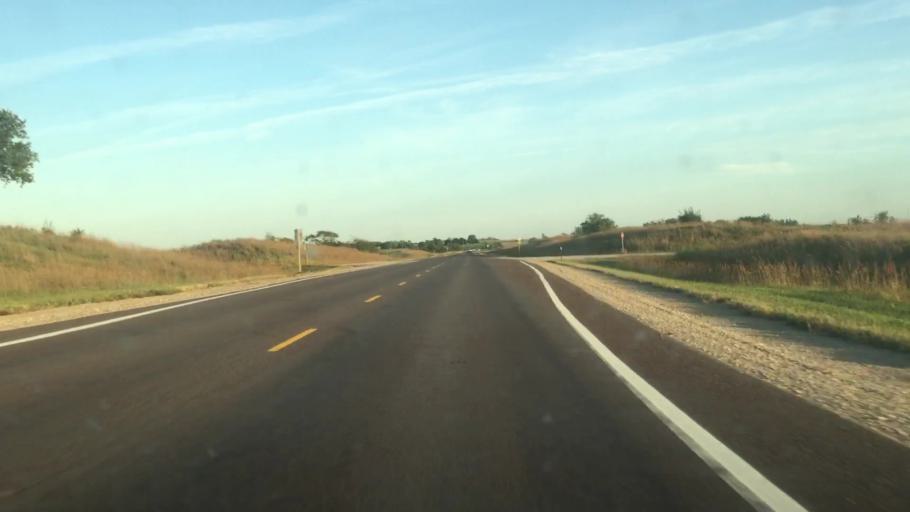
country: US
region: Kansas
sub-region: Atchison County
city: Atchison
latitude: 39.4269
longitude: -95.0734
